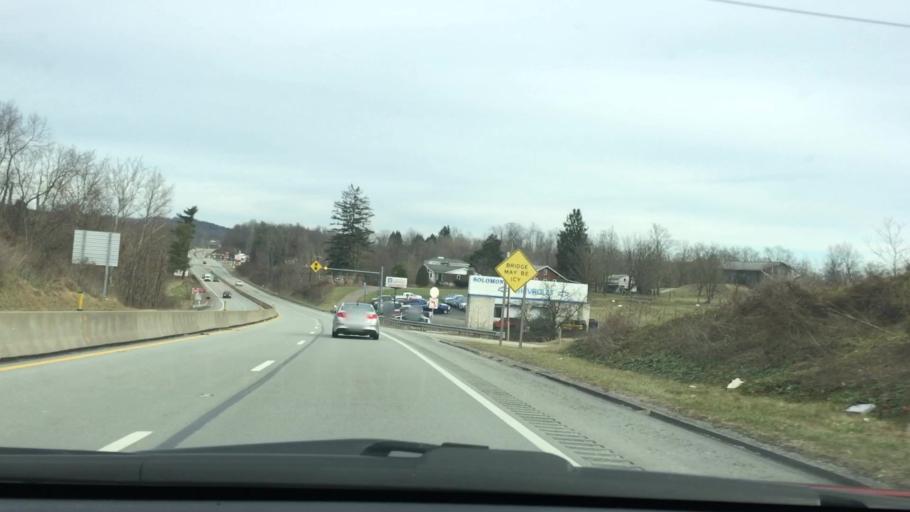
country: US
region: Pennsylvania
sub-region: Fayette County
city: Masontown
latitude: 39.8622
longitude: -79.8958
